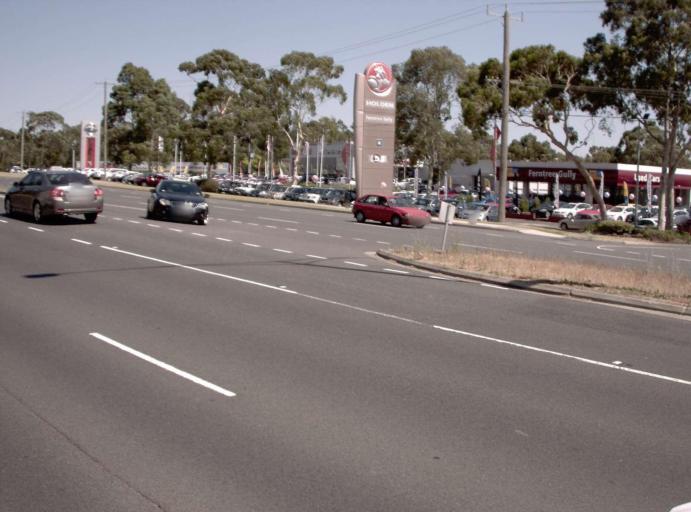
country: AU
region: Victoria
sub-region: Knox
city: Ferntree Gully
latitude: -37.8873
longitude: 145.2862
